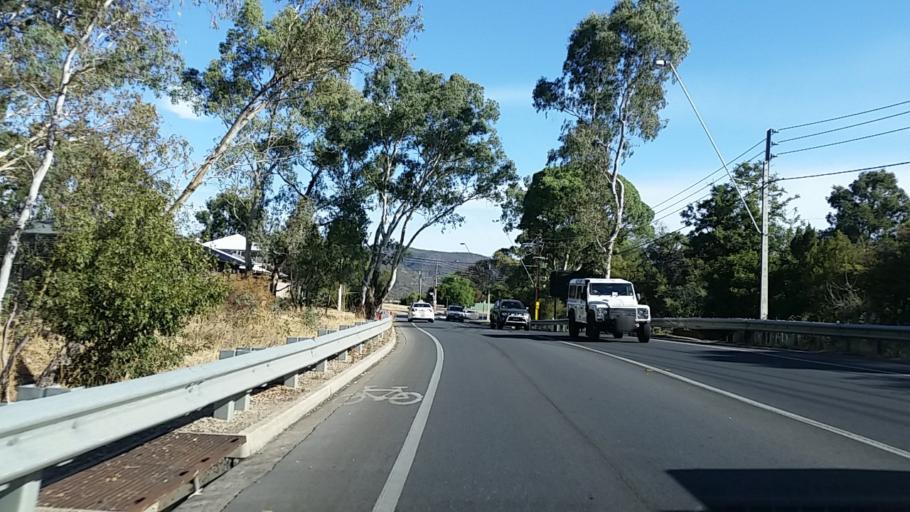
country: AU
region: South Australia
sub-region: Tea Tree Gully
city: Hope Valley
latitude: -34.8409
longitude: 138.7205
